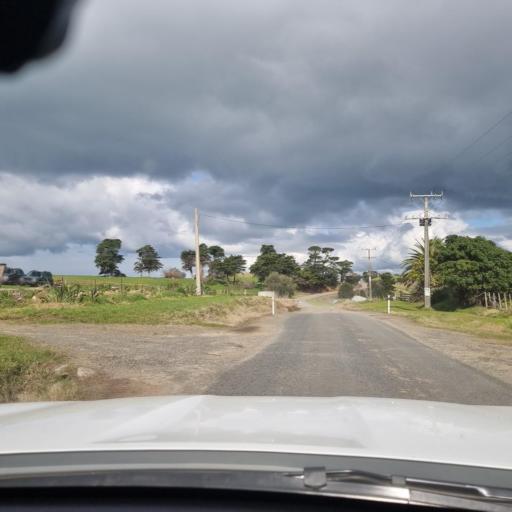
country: NZ
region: Auckland
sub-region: Auckland
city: Wellsford
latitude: -36.3581
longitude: 174.1762
